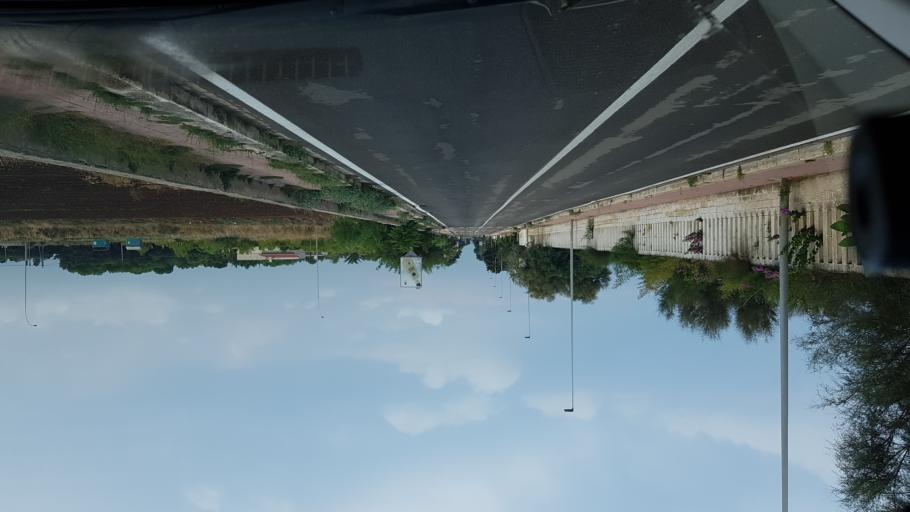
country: IT
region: Apulia
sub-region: Provincia di Brindisi
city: Fasano
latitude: 40.9003
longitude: 17.3607
